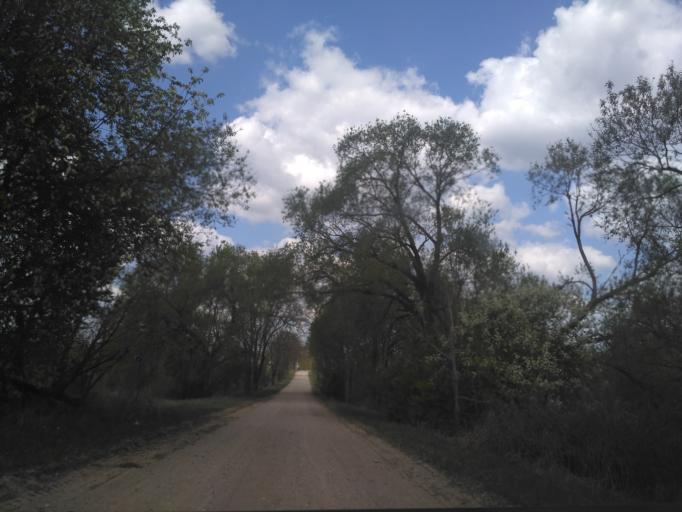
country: BY
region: Minsk
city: Il'ya
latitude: 54.2799
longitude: 27.3037
